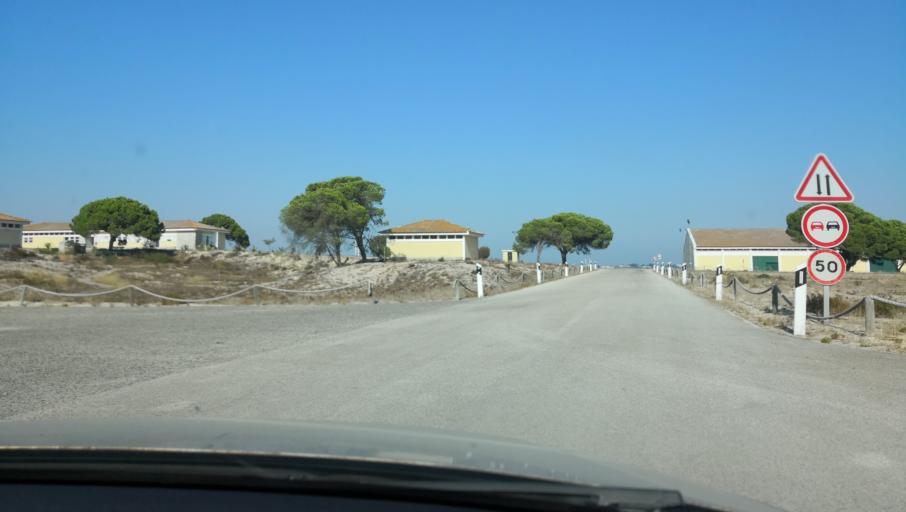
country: PT
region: Setubal
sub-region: Setubal
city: Setubal
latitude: 38.4738
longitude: -8.8731
